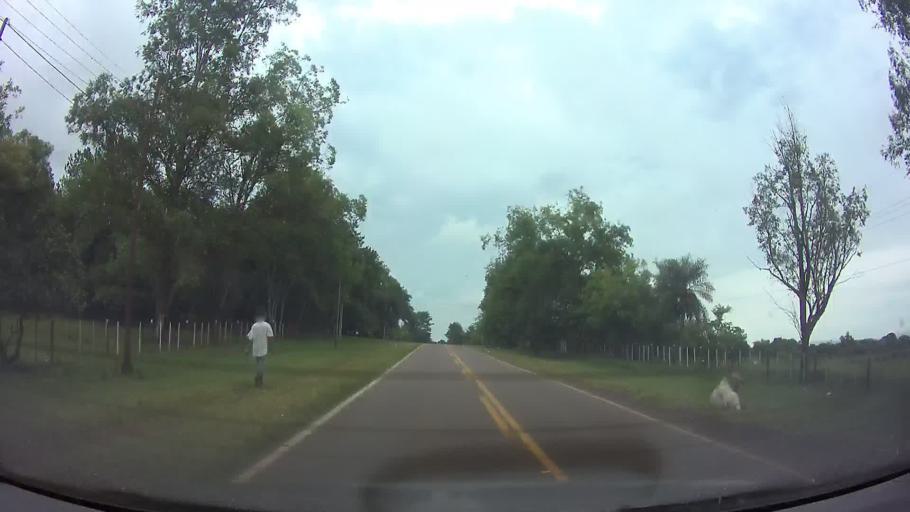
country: PY
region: Paraguari
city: Carapegua
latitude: -25.7866
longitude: -57.2175
